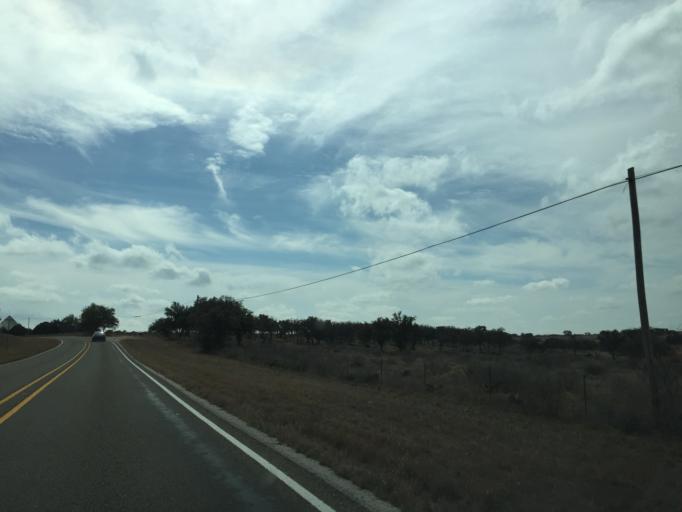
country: US
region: Texas
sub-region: Burnet County
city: Granite Shoals
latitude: 30.4930
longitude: -98.4380
